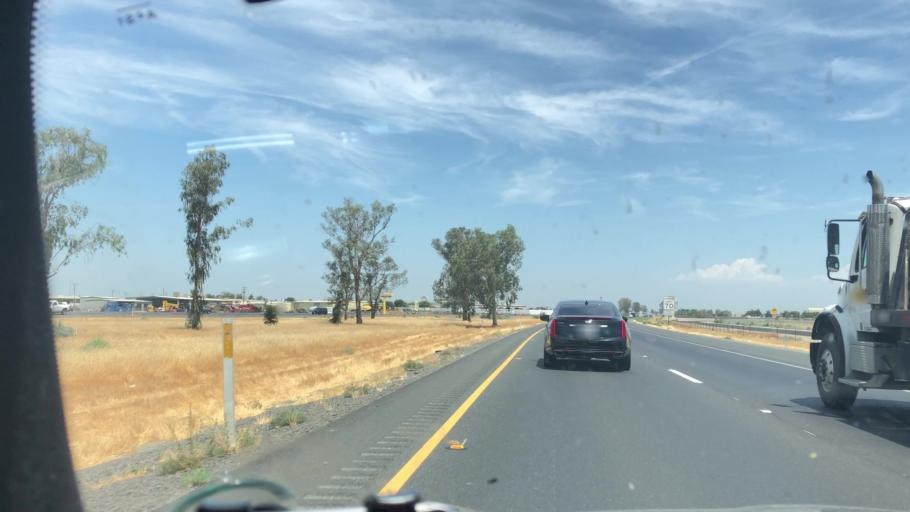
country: US
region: California
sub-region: Tulare County
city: Tulare
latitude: 36.1595
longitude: -119.3325
